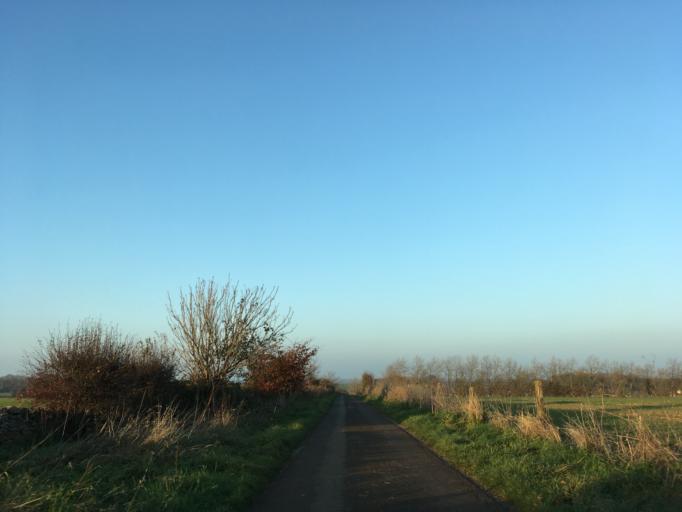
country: GB
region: England
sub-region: Wiltshire
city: Nettleton
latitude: 51.4741
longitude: -2.2820
